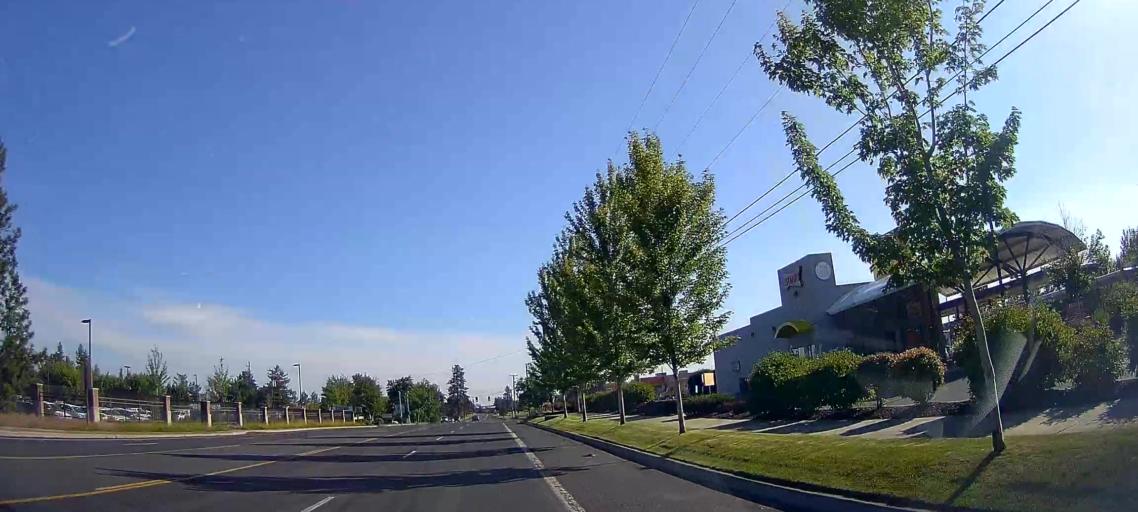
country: US
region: Oregon
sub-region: Deschutes County
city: Bend
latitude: 44.0896
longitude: -121.3055
